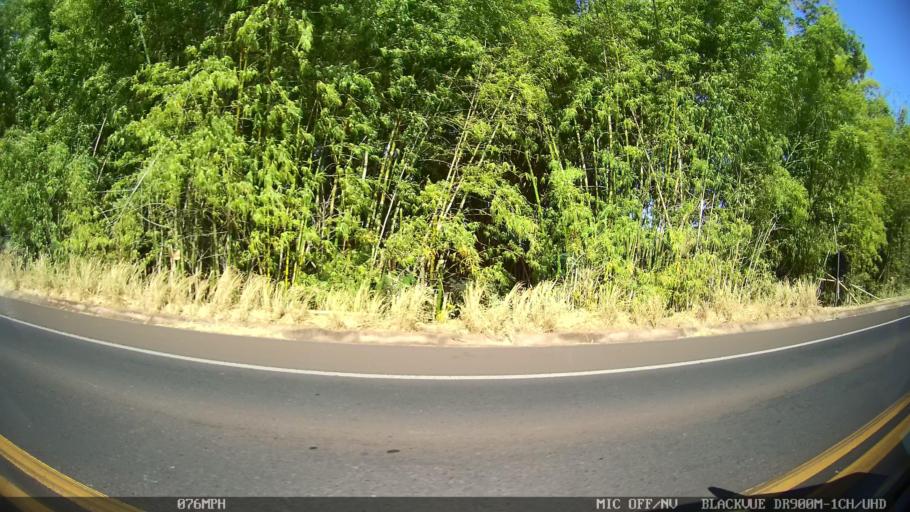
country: BR
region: Sao Paulo
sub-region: Olimpia
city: Olimpia
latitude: -20.6149
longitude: -48.7585
